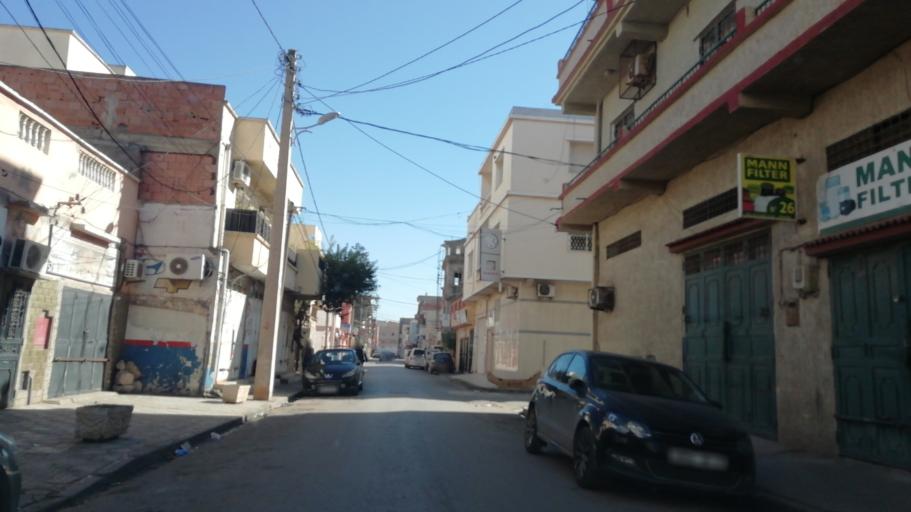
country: DZ
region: Oran
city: Oran
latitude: 35.6942
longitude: -0.6231
